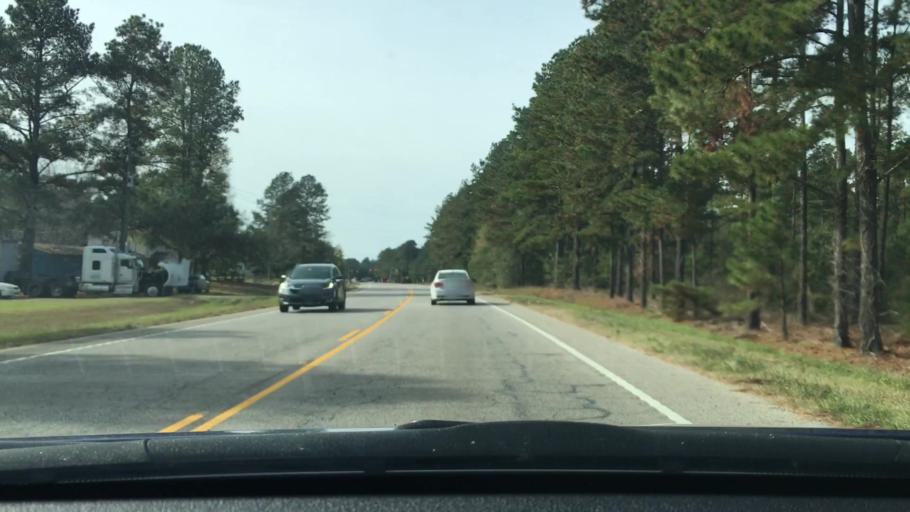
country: US
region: South Carolina
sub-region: Sumter County
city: Cherryvale
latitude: 33.9368
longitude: -80.4488
